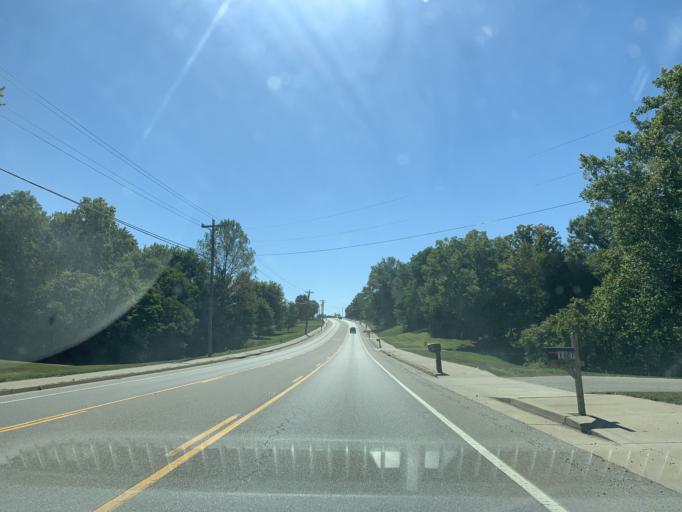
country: US
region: Kentucky
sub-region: Boone County
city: Francisville
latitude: 39.1029
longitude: -84.7227
